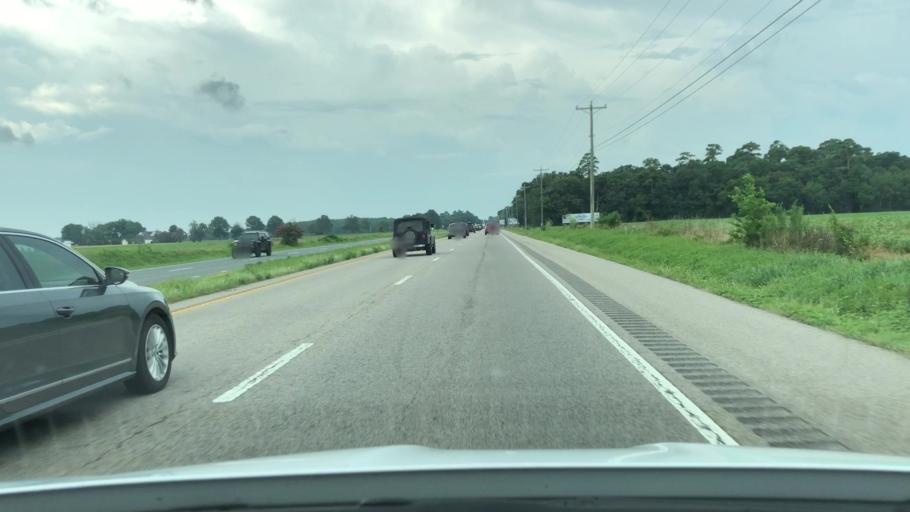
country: US
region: Virginia
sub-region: Northampton County
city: Cape Charles
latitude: 37.2456
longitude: -75.9721
